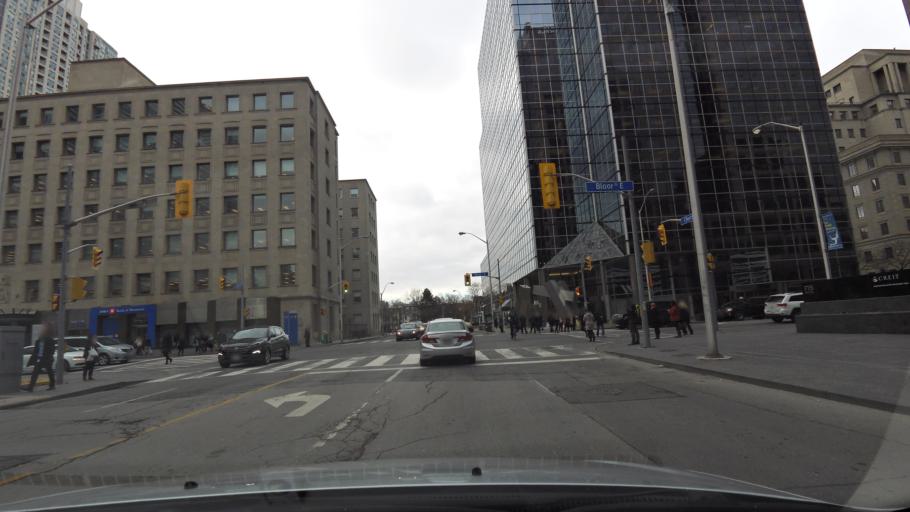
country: CA
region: Ontario
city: Toronto
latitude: 43.6708
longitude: -79.3830
